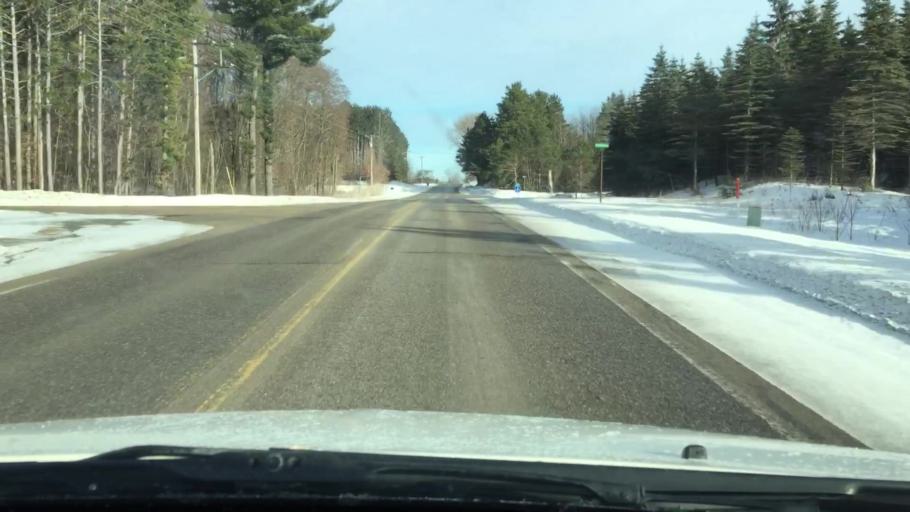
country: US
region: Michigan
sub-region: Kalkaska County
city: Kalkaska
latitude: 44.6408
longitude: -85.2324
